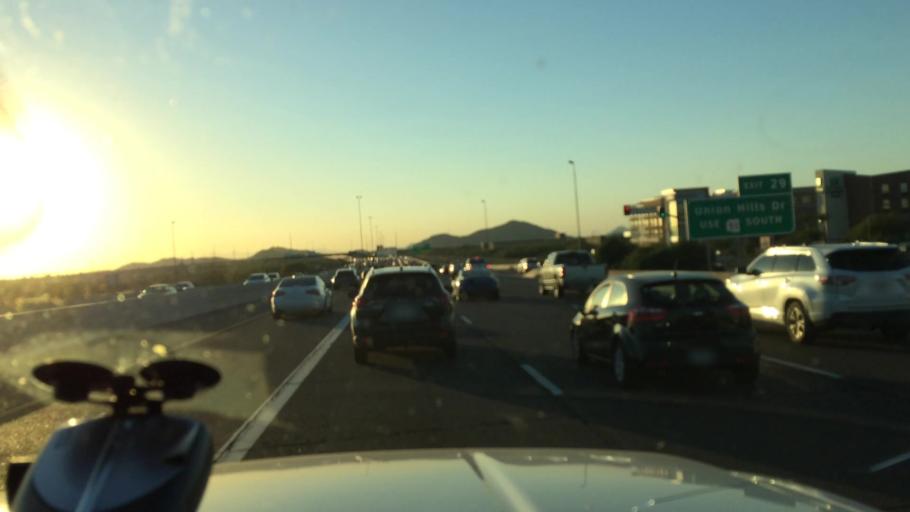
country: US
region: Arizona
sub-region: Maricopa County
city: Paradise Valley
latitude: 33.6735
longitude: -111.9804
